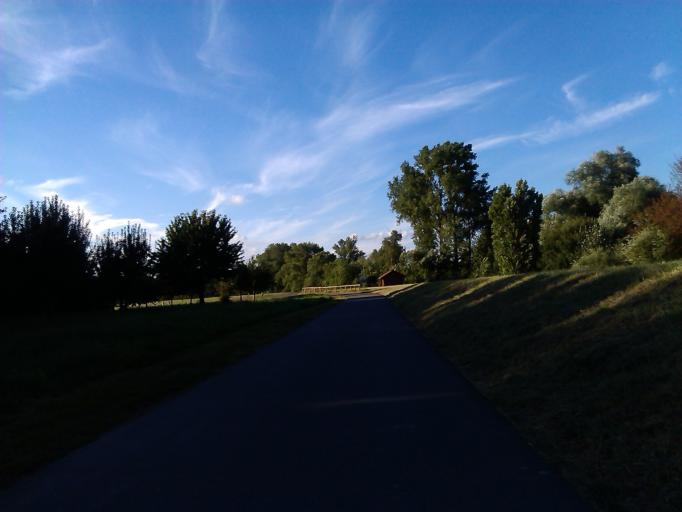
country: DE
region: Rheinland-Pfalz
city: Otterstadt
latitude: 49.3760
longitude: 8.4583
